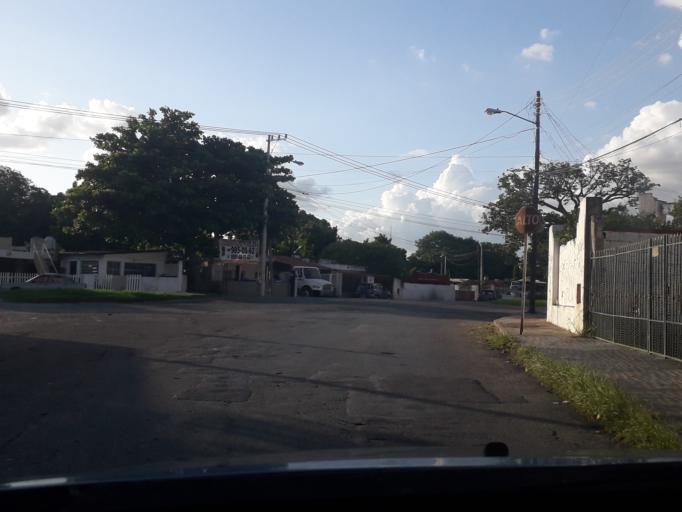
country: MX
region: Yucatan
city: Merida
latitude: 20.9631
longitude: -89.6433
